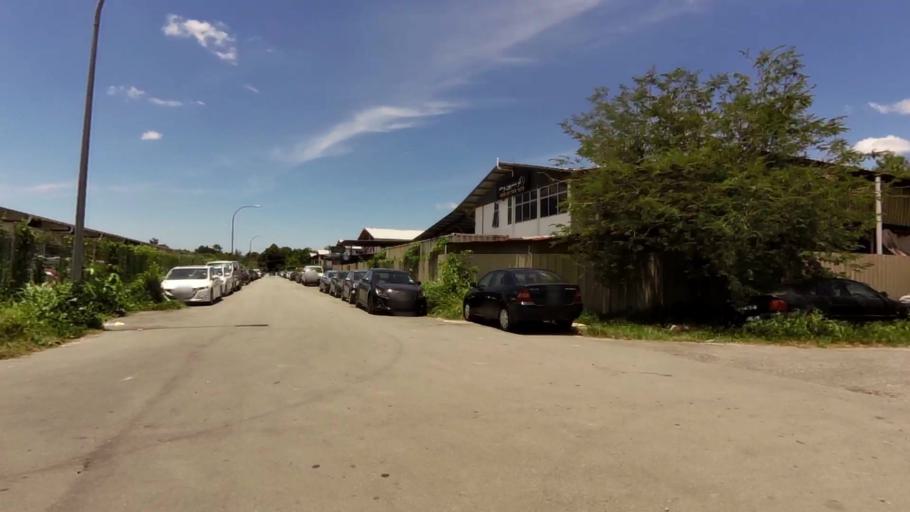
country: BN
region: Brunei and Muara
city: Bandar Seri Begawan
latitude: 4.9402
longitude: 114.9572
